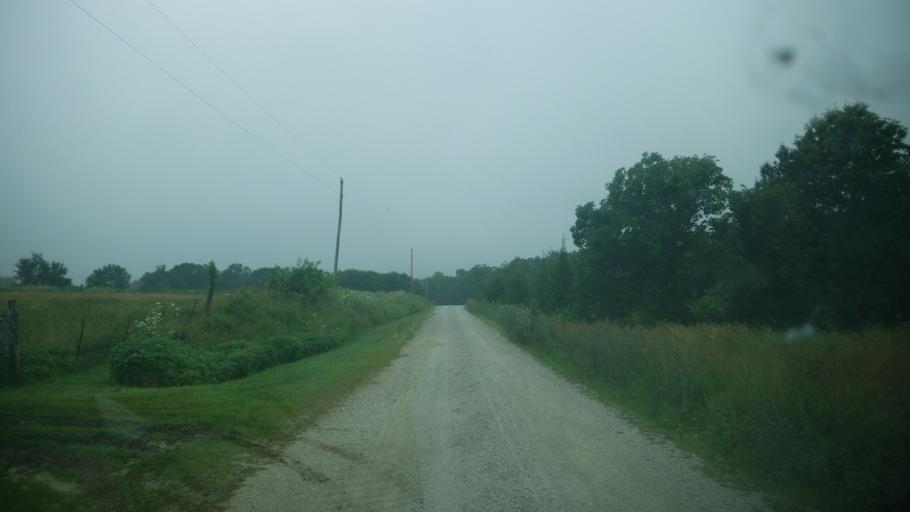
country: US
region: Missouri
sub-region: Audrain County
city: Vandalia
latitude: 39.2726
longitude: -91.3414
